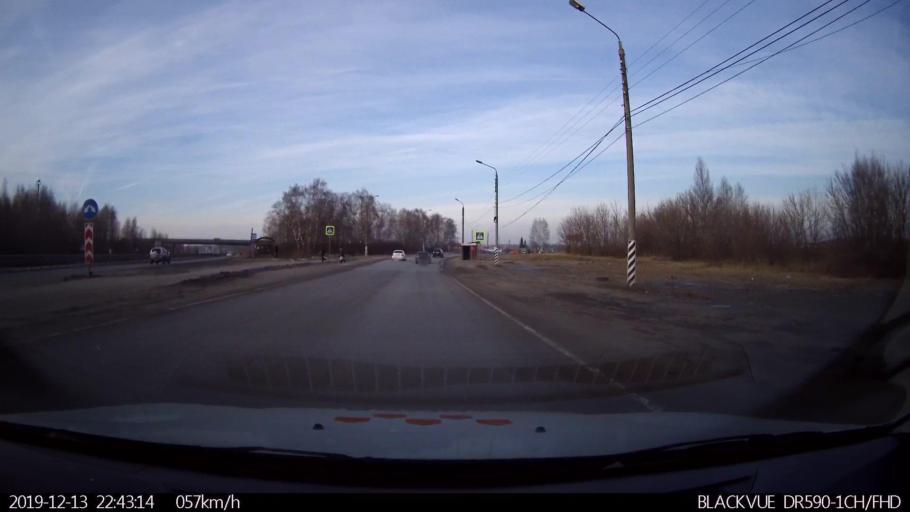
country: RU
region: Nizjnij Novgorod
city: Afonino
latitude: 56.1948
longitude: 44.1257
